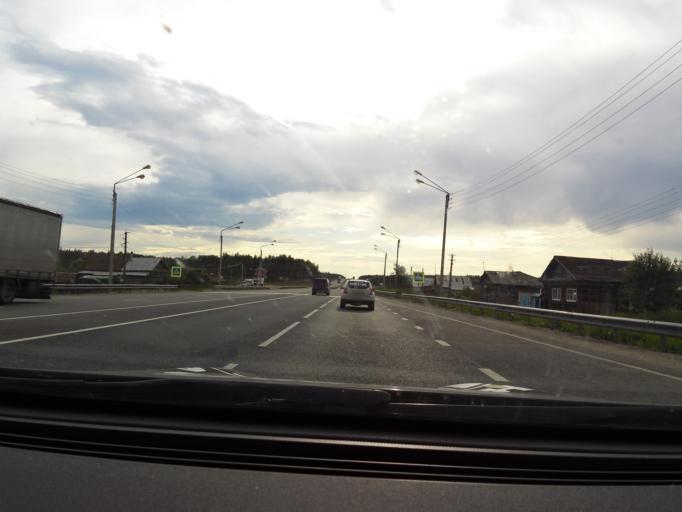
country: RU
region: Vladimir
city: Luknovo
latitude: 56.2376
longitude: 41.9883
